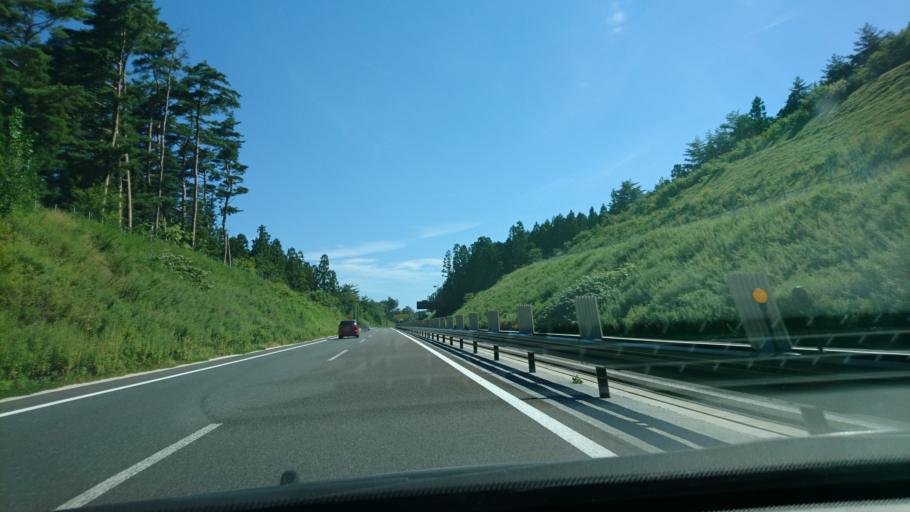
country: JP
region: Iwate
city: Tono
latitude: 39.2960
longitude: 141.4094
